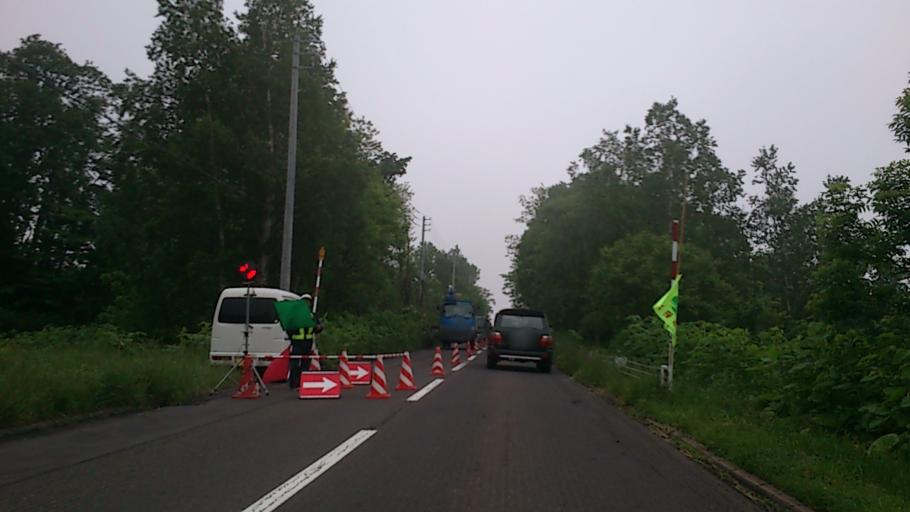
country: JP
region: Hokkaido
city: Niseko Town
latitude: 42.8803
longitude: 140.8280
